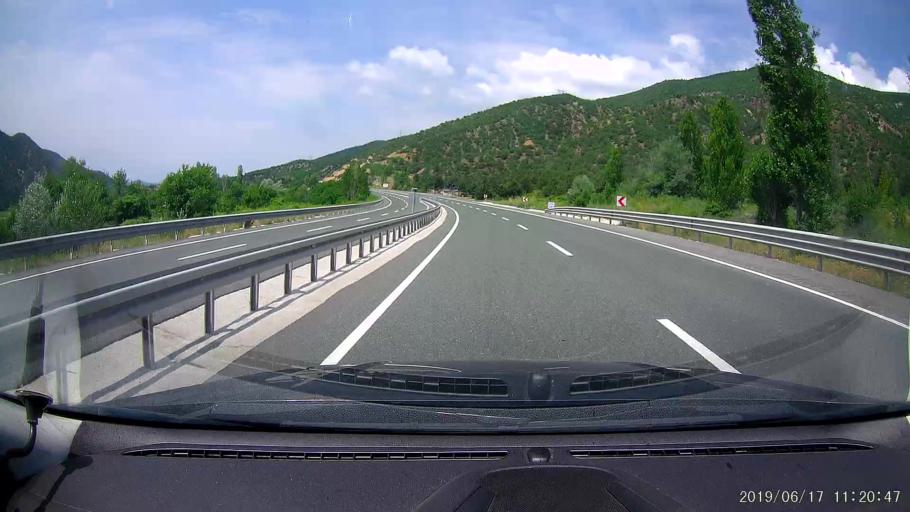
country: TR
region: Cankiri
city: Yaprakli
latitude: 40.9127
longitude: 33.7982
